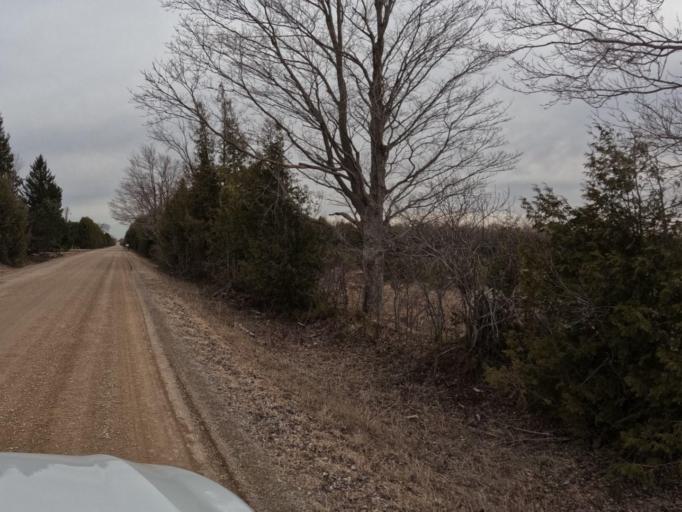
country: CA
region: Ontario
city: Shelburne
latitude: 43.9332
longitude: -80.2583
